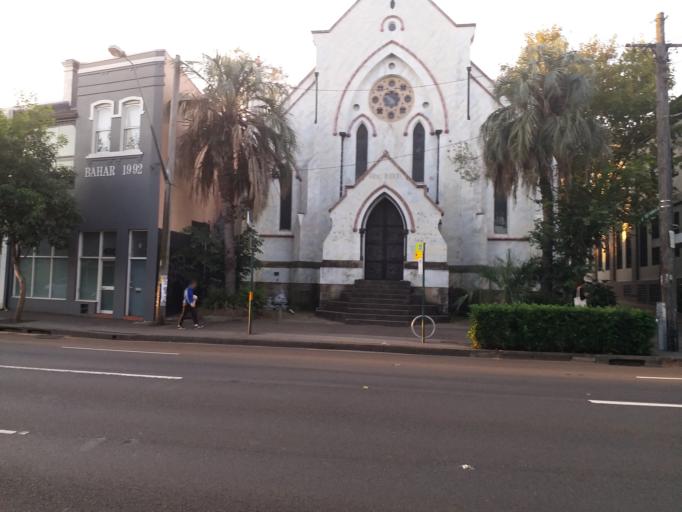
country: AU
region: New South Wales
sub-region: City of Sydney
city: Redfern
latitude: -33.8915
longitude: 151.2118
